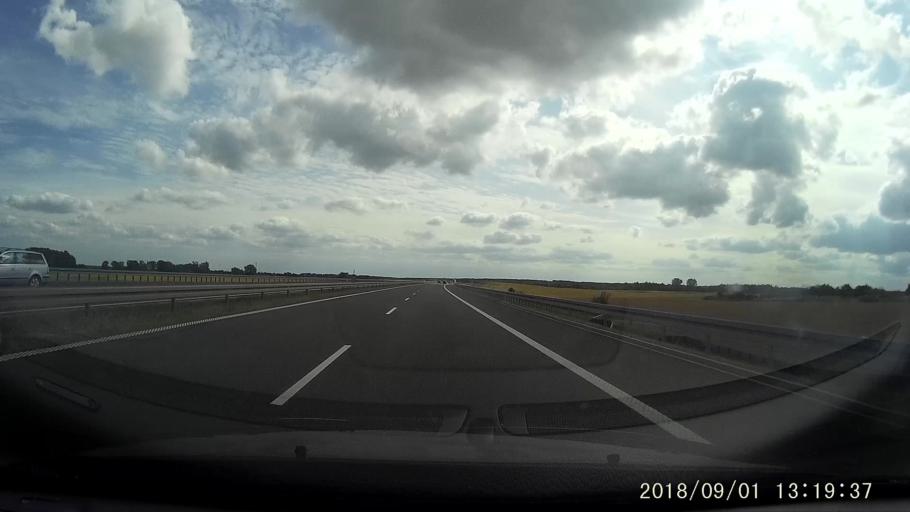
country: PL
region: West Pomeranian Voivodeship
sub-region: Powiat pyrzycki
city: Bielice
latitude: 53.1891
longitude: 14.6894
